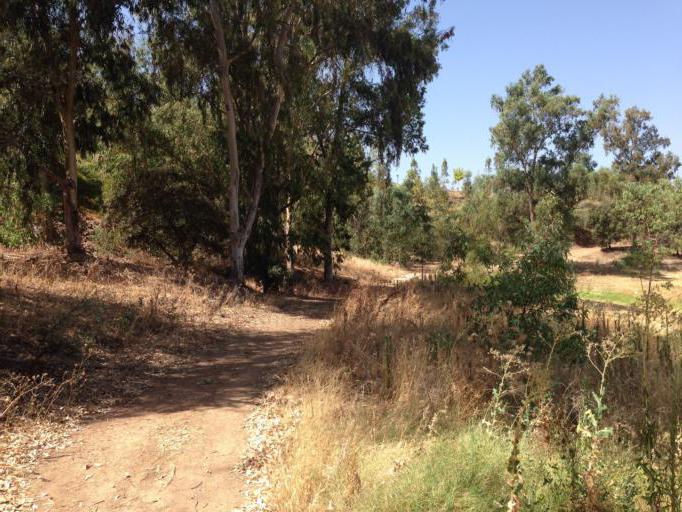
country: ES
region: Extremadura
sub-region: Provincia de Caceres
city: Berrocalejo
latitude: 39.8428
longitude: -5.3745
